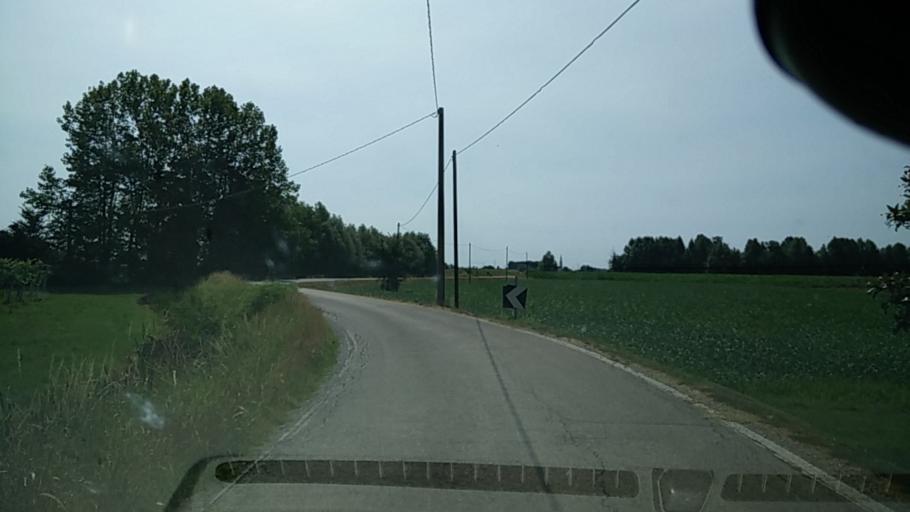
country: IT
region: Veneto
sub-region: Provincia di Treviso
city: Fontanelle
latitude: 45.8273
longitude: 12.4614
